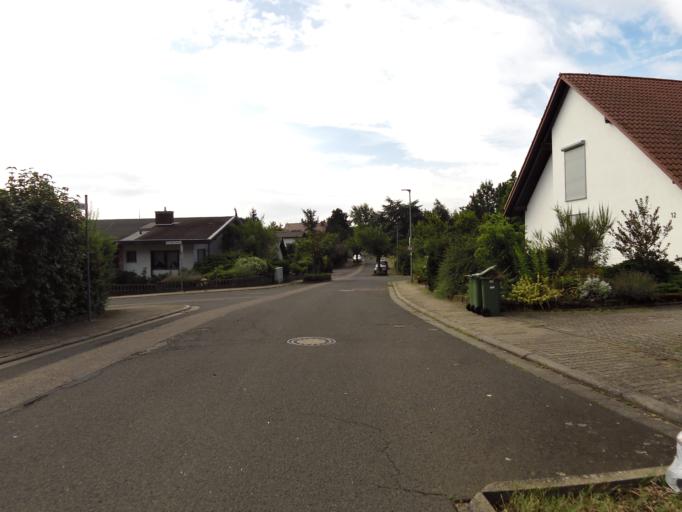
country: DE
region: Rheinland-Pfalz
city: Weisenheim am Berg
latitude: 49.5110
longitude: 8.1520
